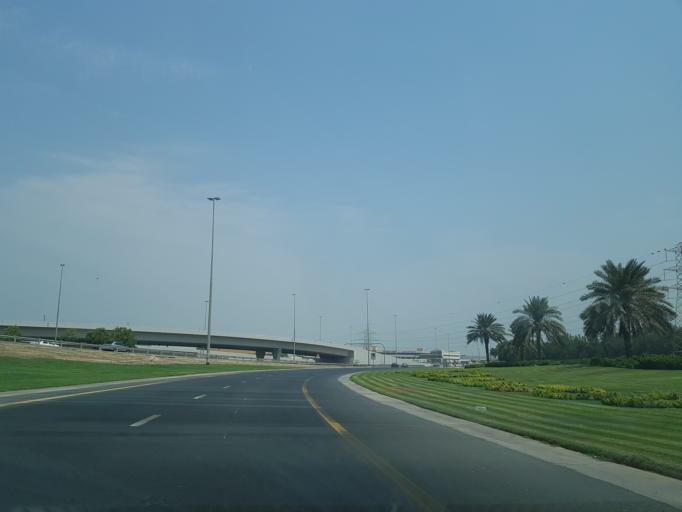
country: AE
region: Ash Shariqah
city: Sharjah
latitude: 25.2183
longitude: 55.3773
